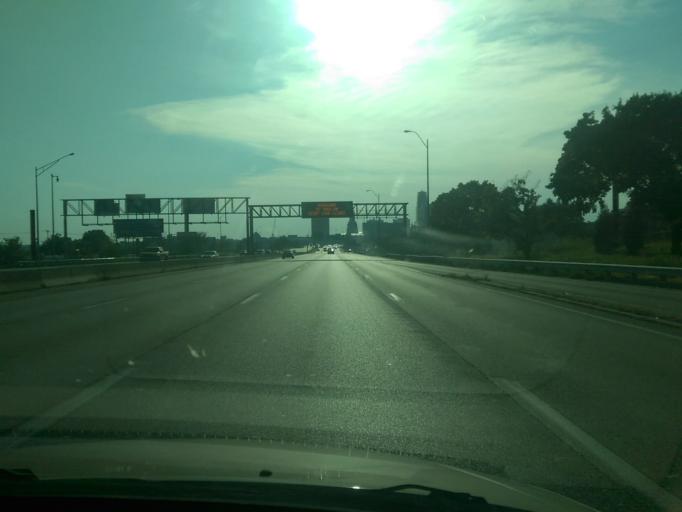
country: US
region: Missouri
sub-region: Jackson County
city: Kansas City
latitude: 39.0961
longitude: -94.5581
